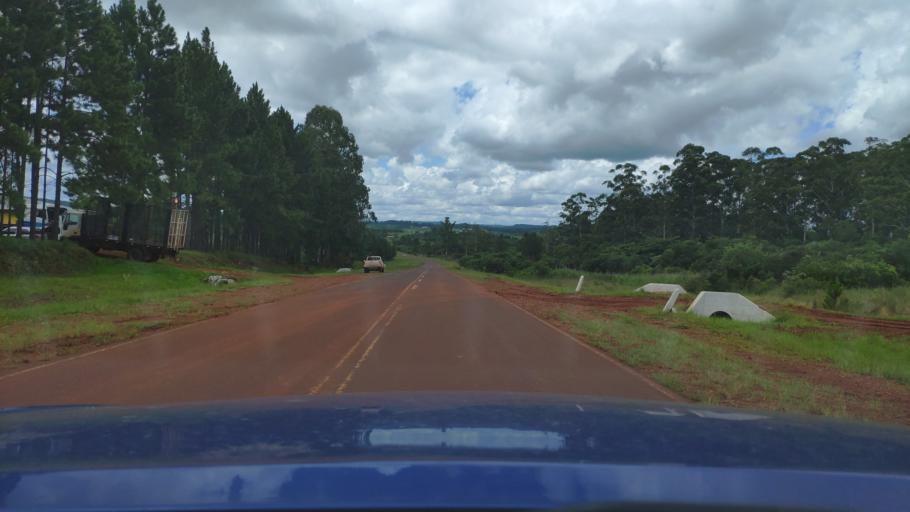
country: AR
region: Misiones
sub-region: Departamento de San Javier
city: San Javier
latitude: -27.8543
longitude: -55.2494
